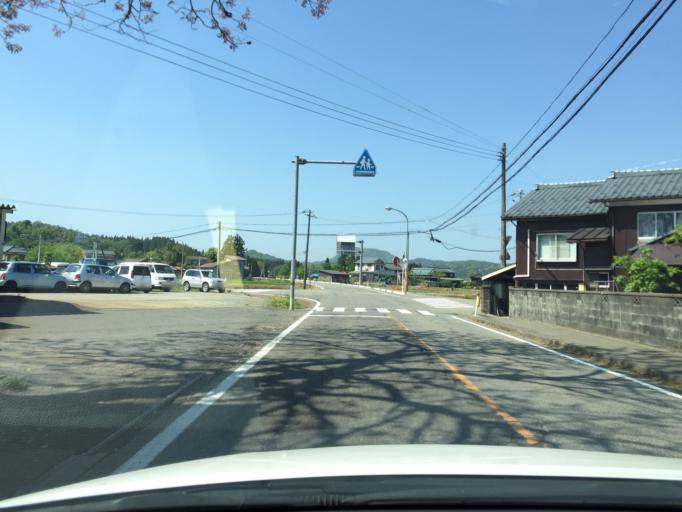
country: JP
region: Niigata
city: Muramatsu
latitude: 37.6726
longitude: 139.1483
